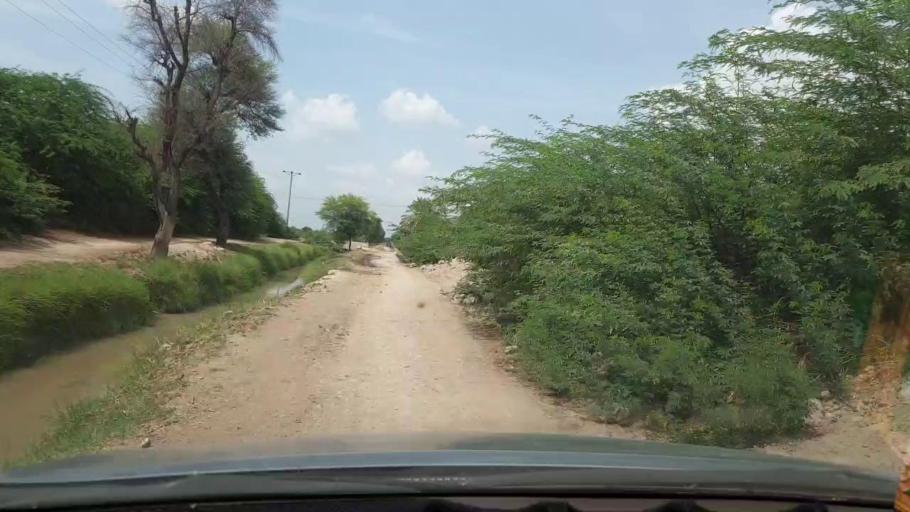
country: PK
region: Sindh
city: Khairpur
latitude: 27.4769
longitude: 68.8508
